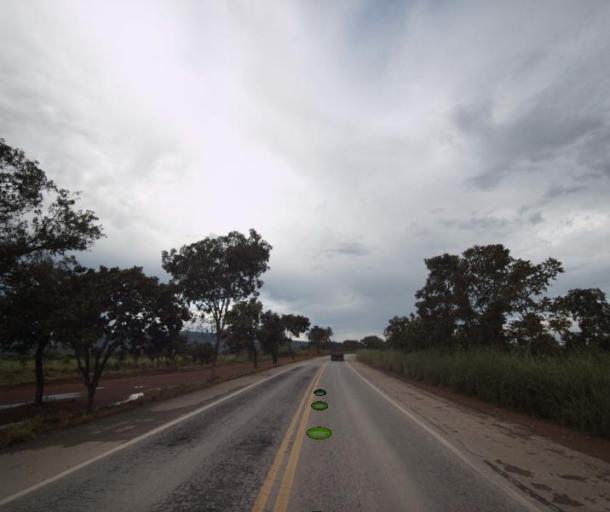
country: BR
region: Goias
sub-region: Porangatu
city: Porangatu
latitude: -13.5796
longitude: -49.0417
